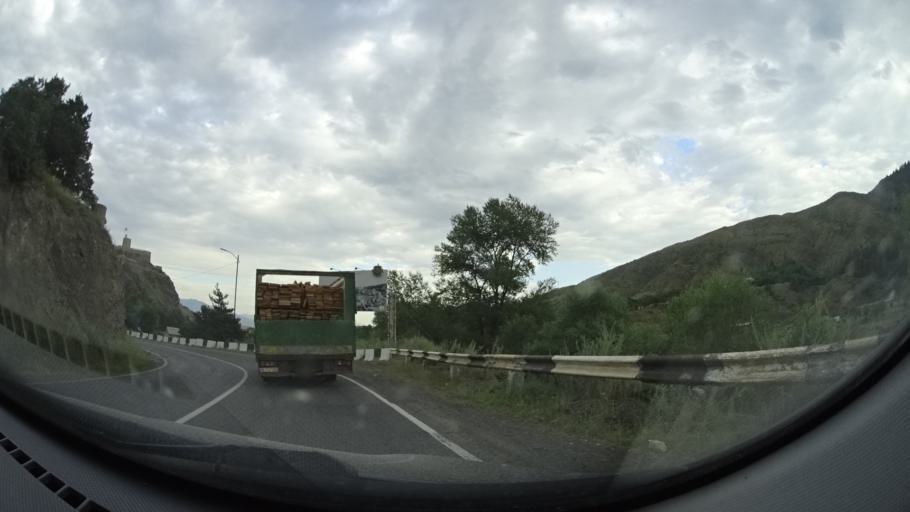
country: GE
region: Samtskhe-Javakheti
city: Akhaltsikhe
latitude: 41.6405
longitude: 42.9701
